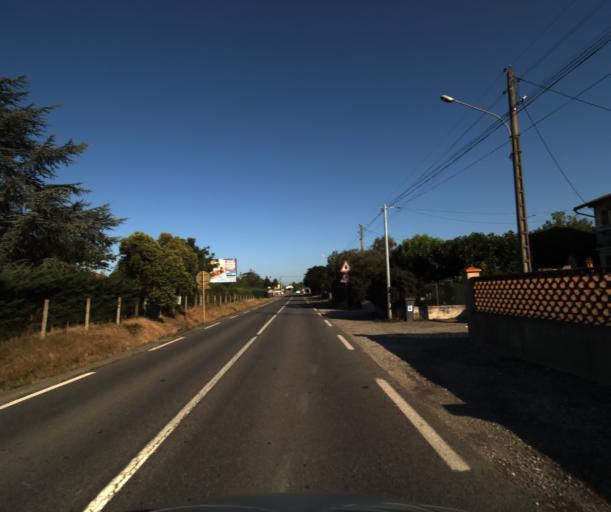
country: FR
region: Midi-Pyrenees
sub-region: Departement de la Haute-Garonne
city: Labarthe-sur-Leze
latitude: 43.4575
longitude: 1.3826
